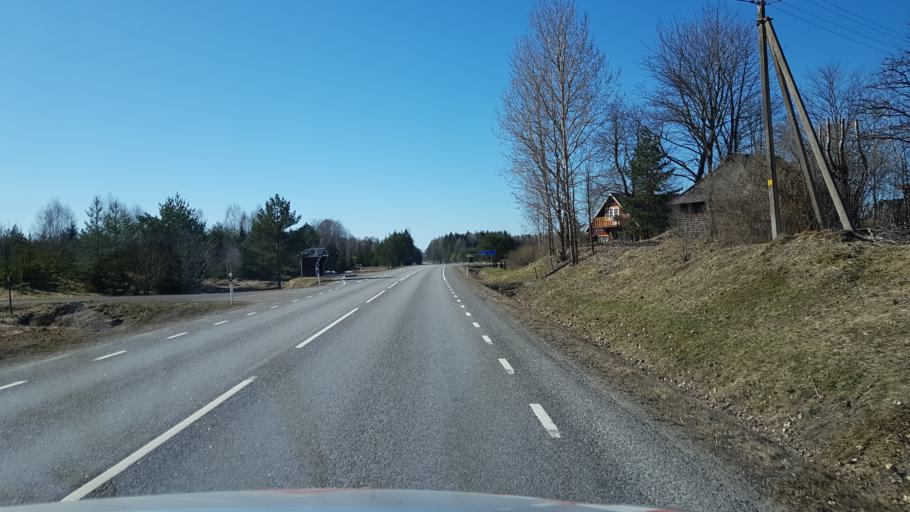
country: EE
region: Ida-Virumaa
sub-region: Aseri vald
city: Aseri
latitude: 59.3484
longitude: 26.7631
